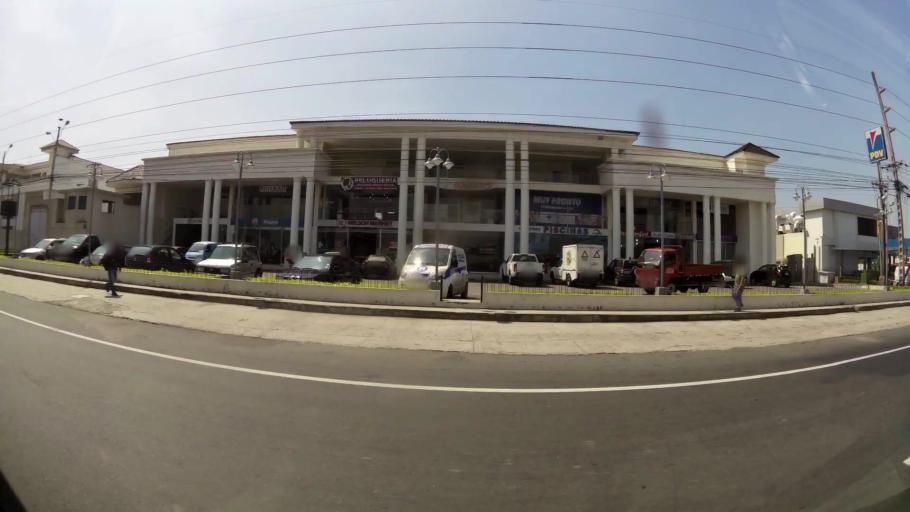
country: EC
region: Guayas
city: Eloy Alfaro
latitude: -2.0548
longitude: -79.8774
